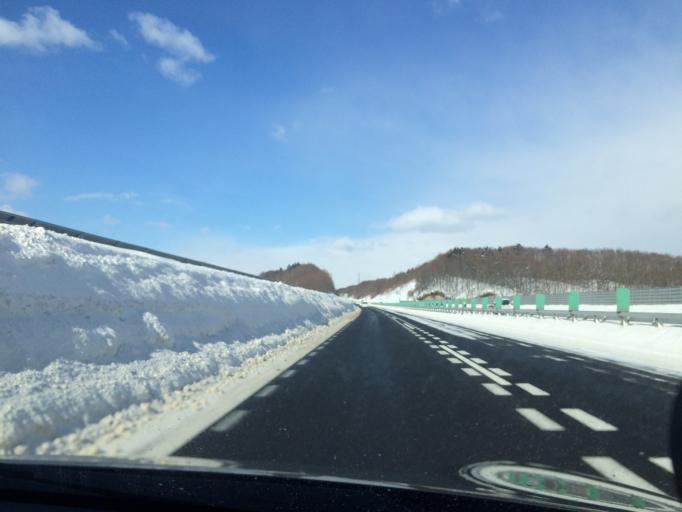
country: JP
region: Hokkaido
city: Kitahiroshima
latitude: 42.9222
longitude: 141.5425
